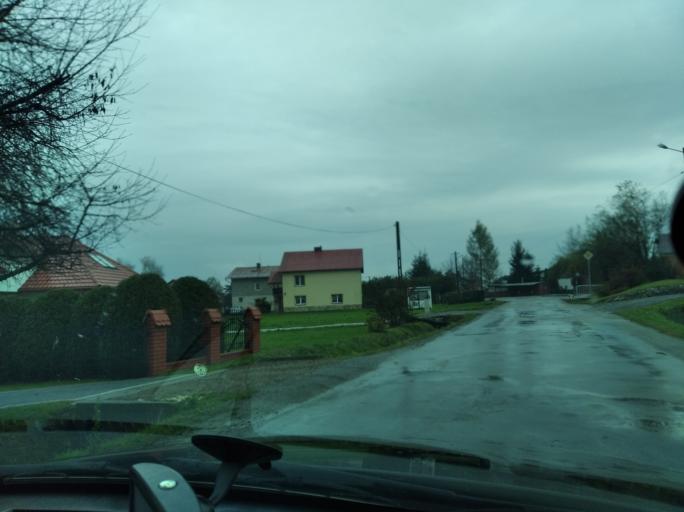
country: PL
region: Subcarpathian Voivodeship
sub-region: Powiat strzyzowski
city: Czudec
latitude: 49.9308
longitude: 21.8481
